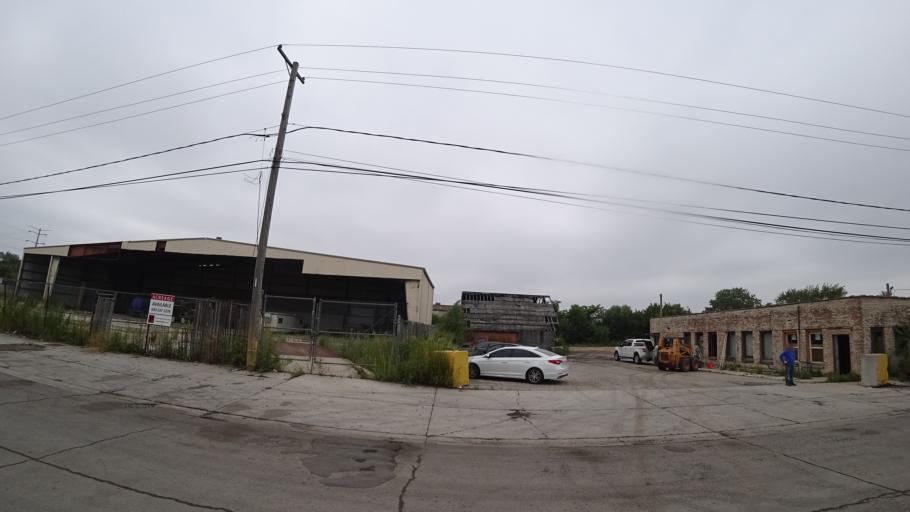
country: US
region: Illinois
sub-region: Cook County
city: Chicago
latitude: 41.8471
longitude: -87.6635
